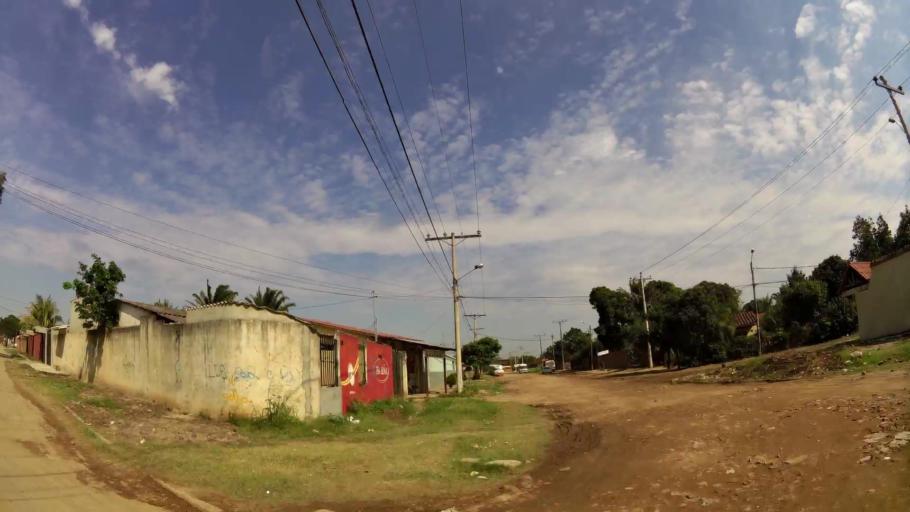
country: BO
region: Santa Cruz
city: Santa Cruz de la Sierra
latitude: -17.7250
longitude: -63.1527
